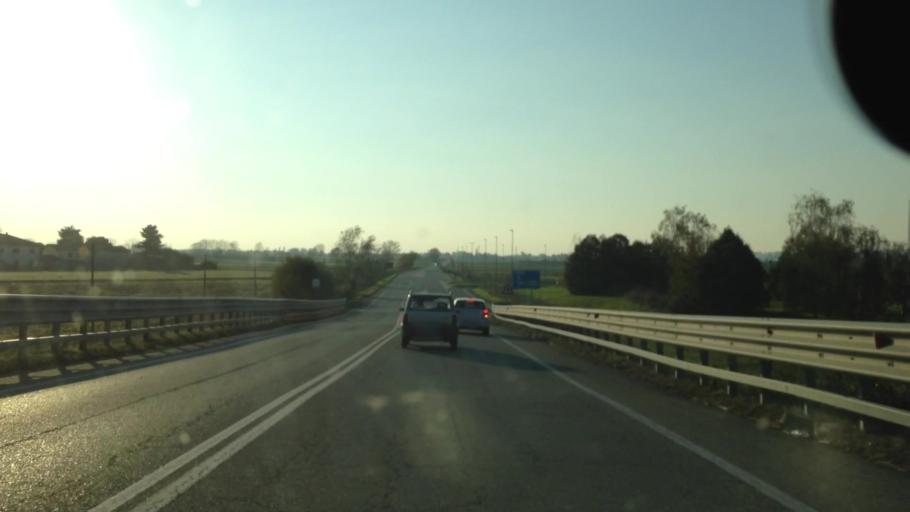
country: IT
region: Piedmont
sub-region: Provincia di Vercelli
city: Borgo d'Ale
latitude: 45.3200
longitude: 8.0694
